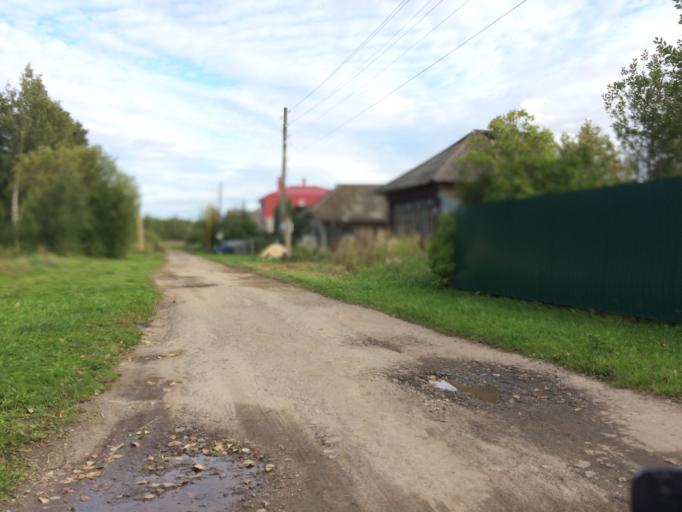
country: RU
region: Mariy-El
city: Yoshkar-Ola
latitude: 56.6525
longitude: 48.0149
